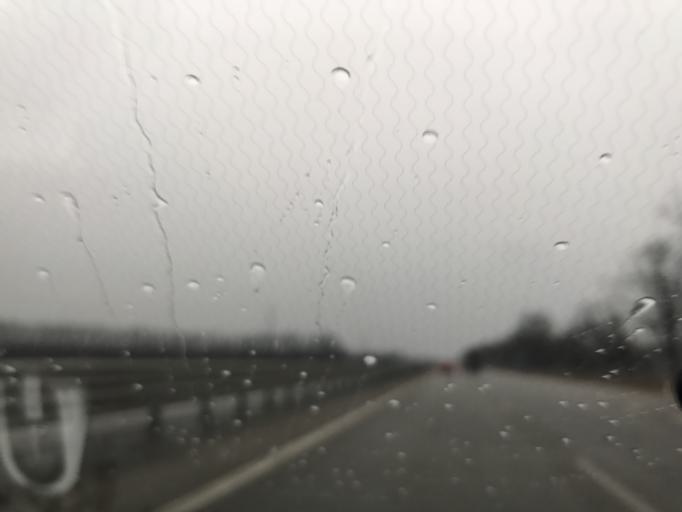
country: RU
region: Krasnodarskiy
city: Kislyakovskaya
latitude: 46.3597
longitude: 39.7641
